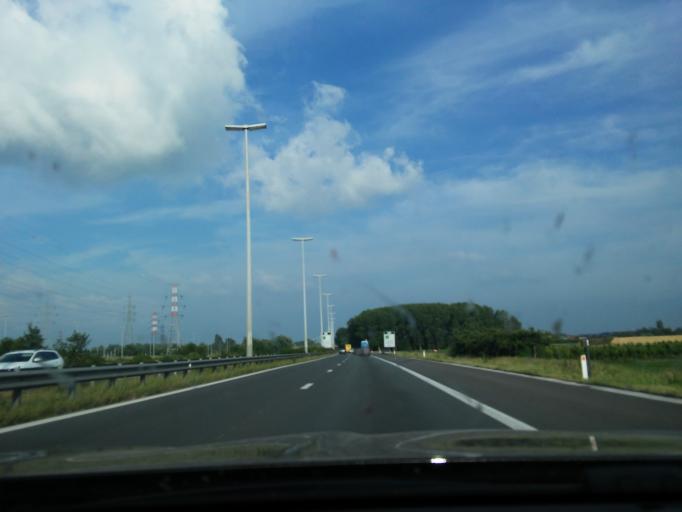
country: BE
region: Flanders
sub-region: Provincie Antwerpen
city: Zwijndrecht
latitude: 51.2310
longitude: 4.3180
